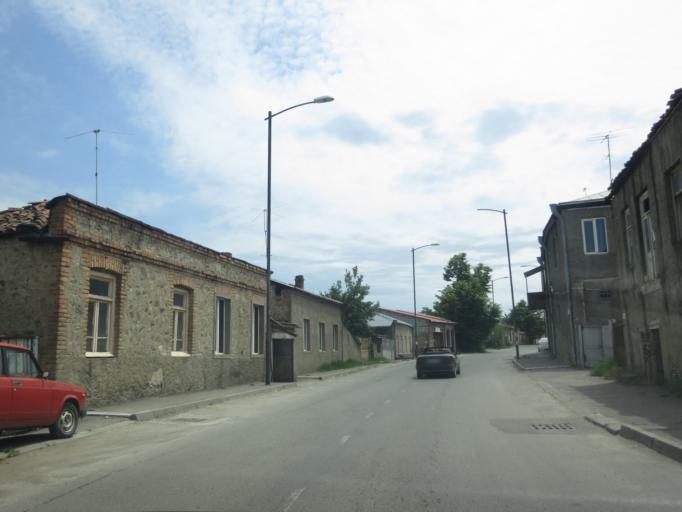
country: GE
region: Kakheti
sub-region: Telavi
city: Telavi
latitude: 41.9252
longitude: 45.4569
